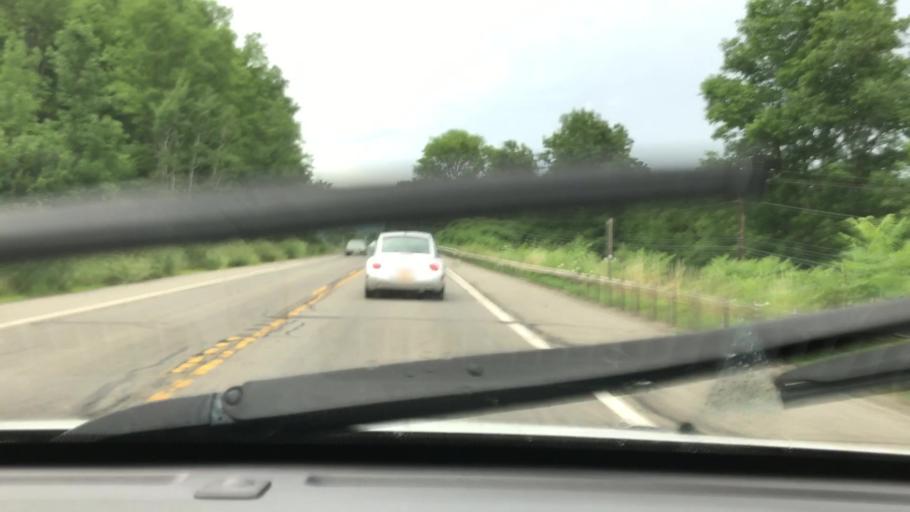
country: US
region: New York
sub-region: Cattaraugus County
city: Salamanca
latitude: 42.2389
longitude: -78.6405
